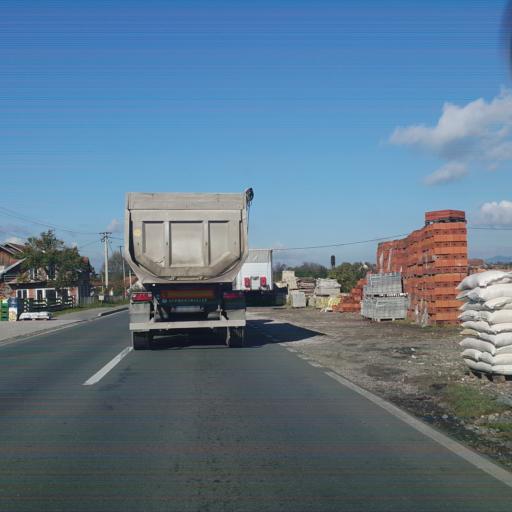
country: RS
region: Central Serbia
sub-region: Raski Okrug
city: Vrnjacka Banja
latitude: 43.6364
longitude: 20.9338
